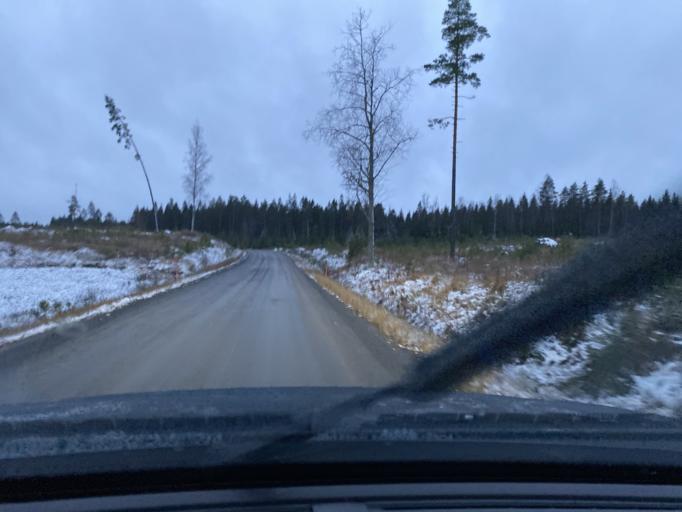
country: FI
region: Pirkanmaa
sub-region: Lounais-Pirkanmaa
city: Punkalaidun
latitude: 61.1601
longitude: 22.9456
